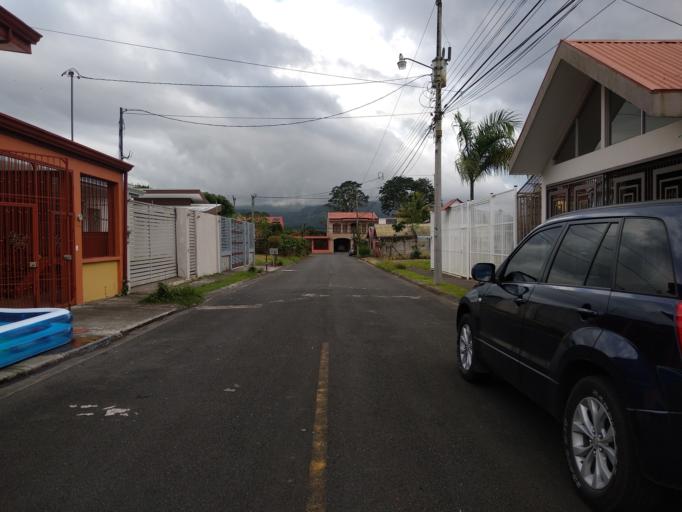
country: CR
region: Cartago
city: Turrialba
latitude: 9.8980
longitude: -83.6735
